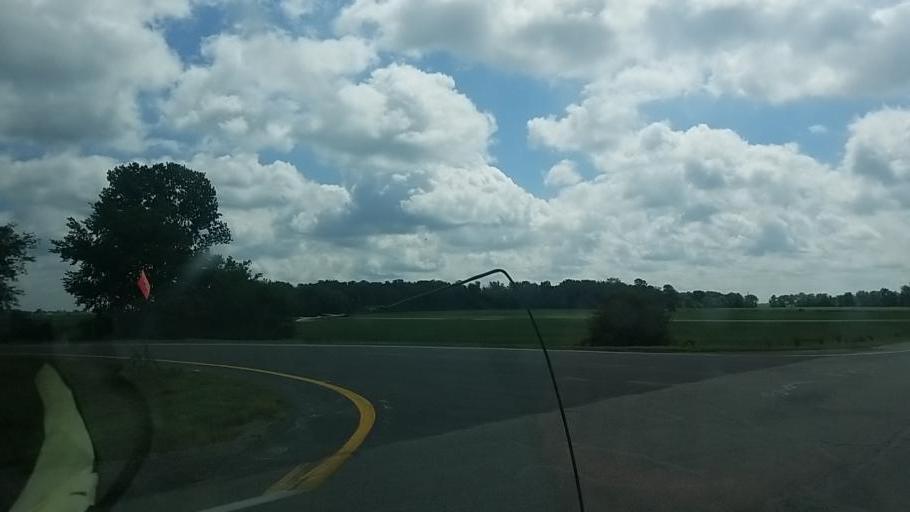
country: US
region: Ohio
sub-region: Madison County
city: Bethel
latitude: 39.6953
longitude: -83.4558
